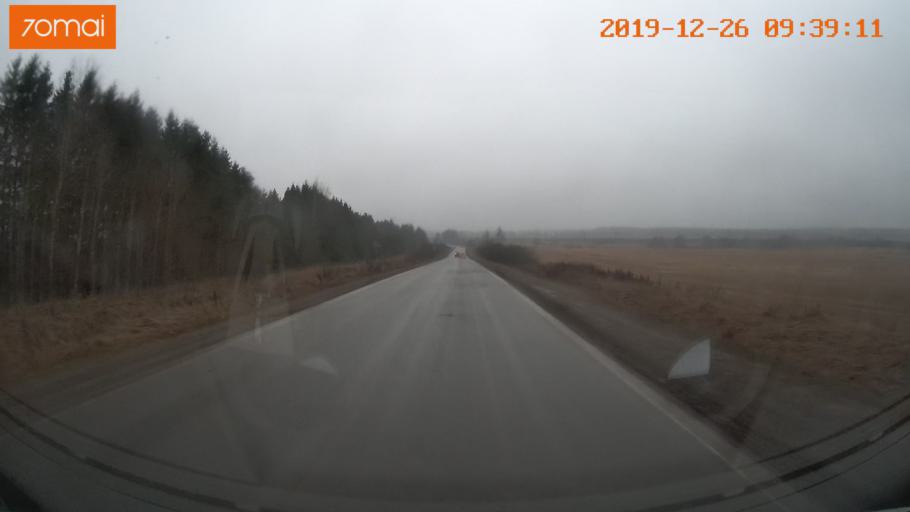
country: RU
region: Vologda
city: Vologda
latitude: 59.1519
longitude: 40.0296
